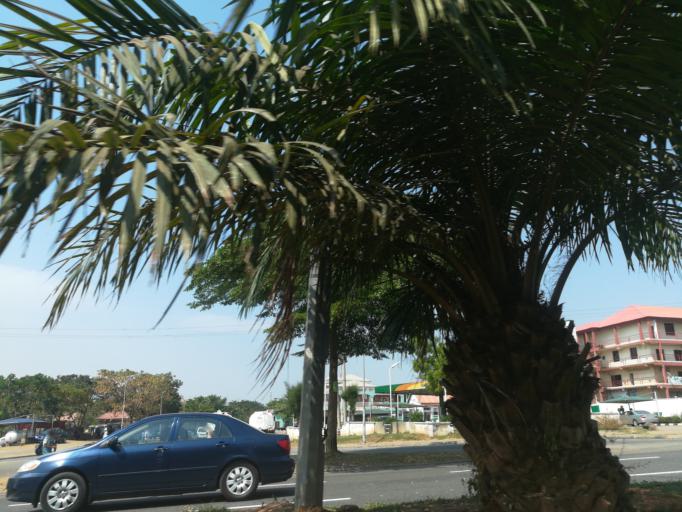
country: NG
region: Abuja Federal Capital Territory
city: Abuja
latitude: 9.0670
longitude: 7.4372
